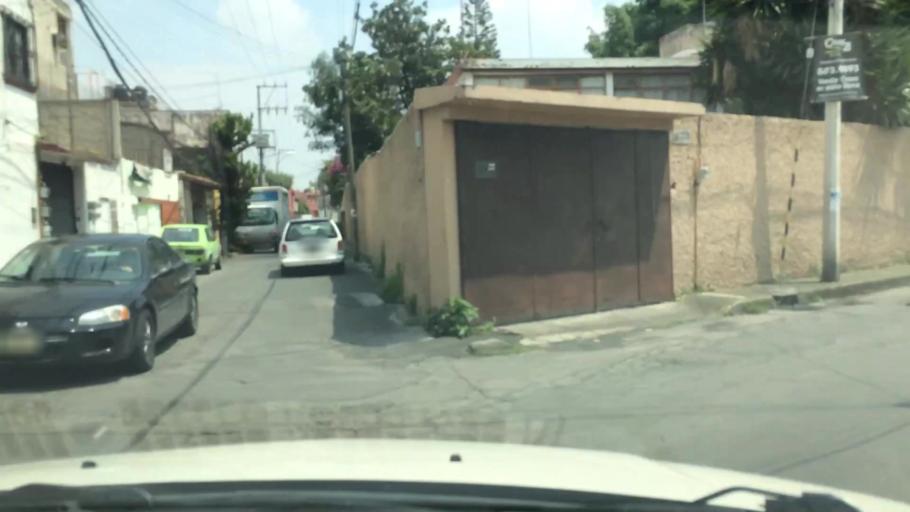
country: MX
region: Mexico City
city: Xochimilco
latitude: 19.2739
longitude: -99.1299
